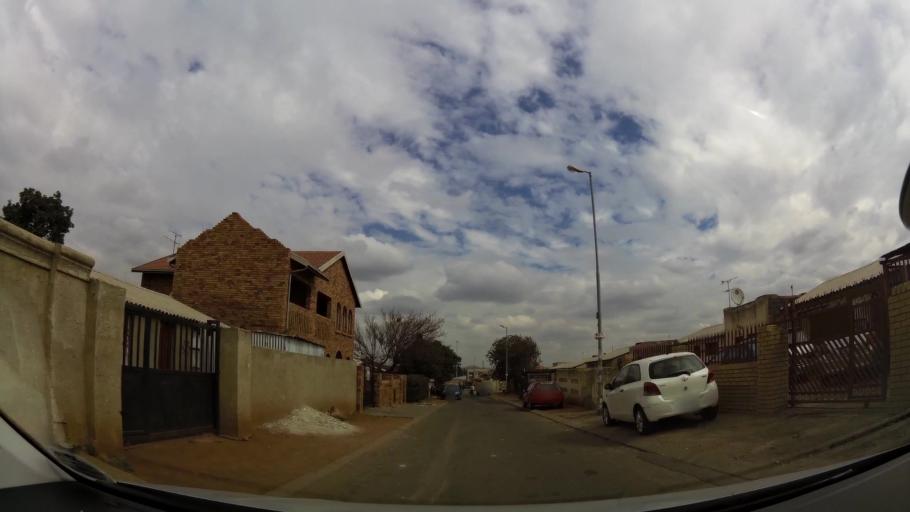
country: ZA
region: Gauteng
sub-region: City of Johannesburg Metropolitan Municipality
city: Soweto
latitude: -26.2824
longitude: 27.8564
